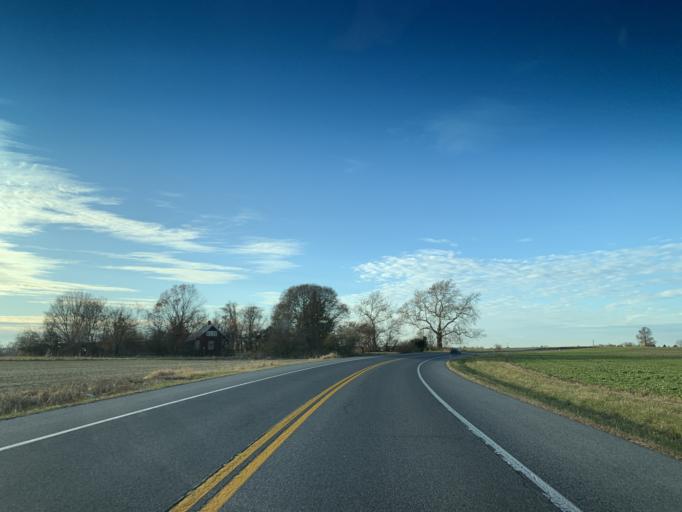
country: US
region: Maryland
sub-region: Kent County
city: Chestertown
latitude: 39.2482
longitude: -76.0741
